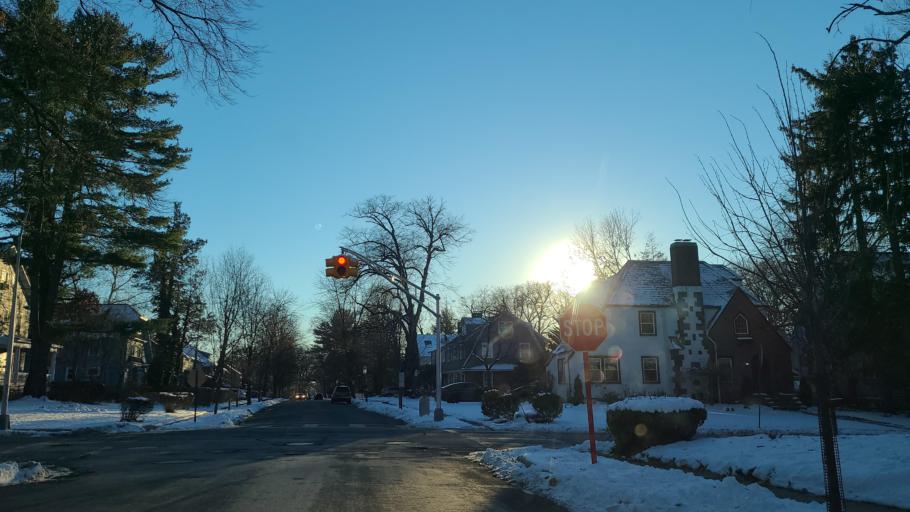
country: US
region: New Jersey
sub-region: Essex County
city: South Orange
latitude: 40.7568
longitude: -74.2545
